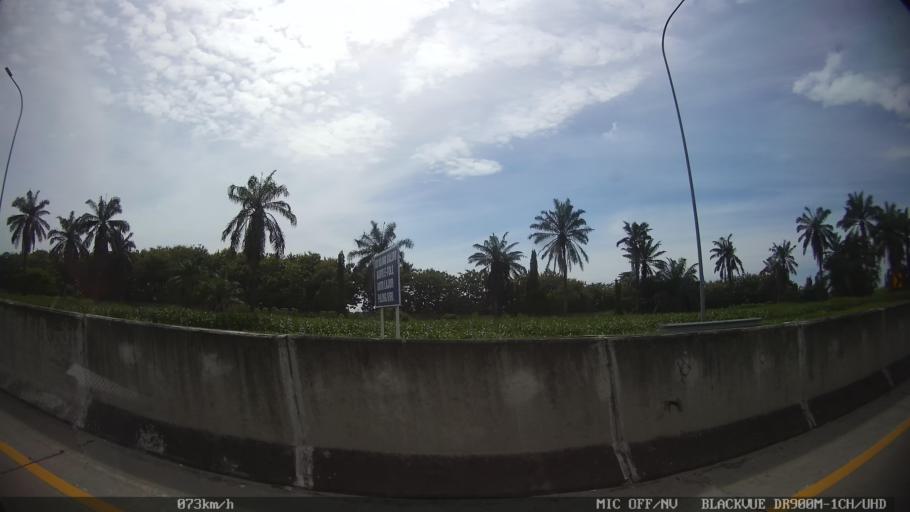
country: ID
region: North Sumatra
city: Medan
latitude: 3.6326
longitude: 98.6351
